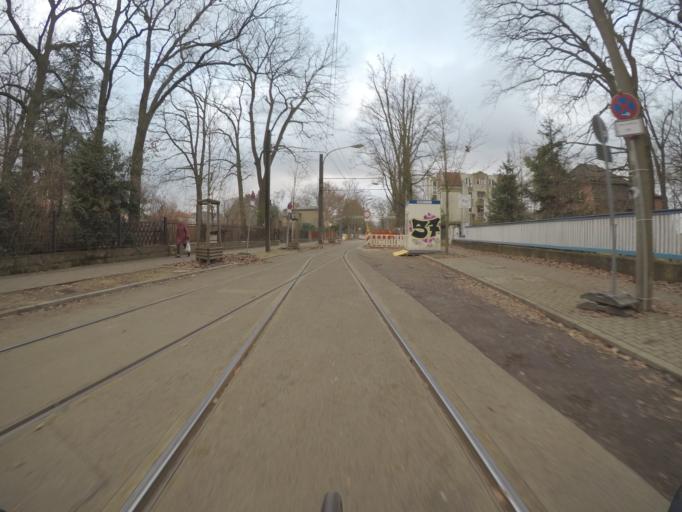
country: DE
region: Berlin
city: Grunau
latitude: 52.4210
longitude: 13.5881
